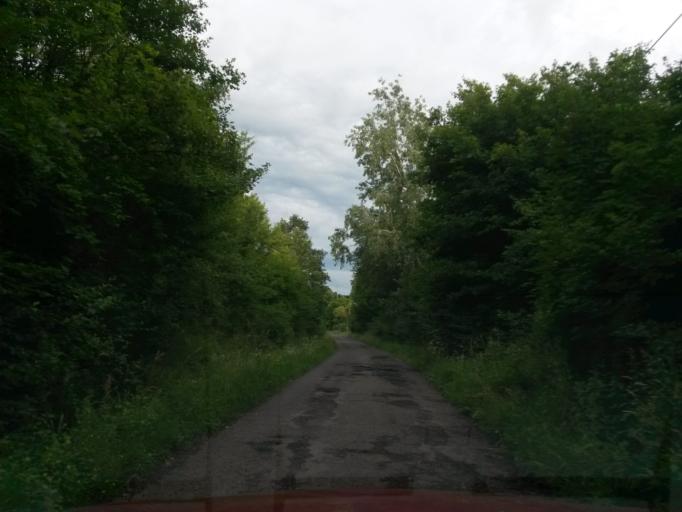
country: SK
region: Banskobystricky
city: Velky Krtis
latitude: 48.3279
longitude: 19.4441
